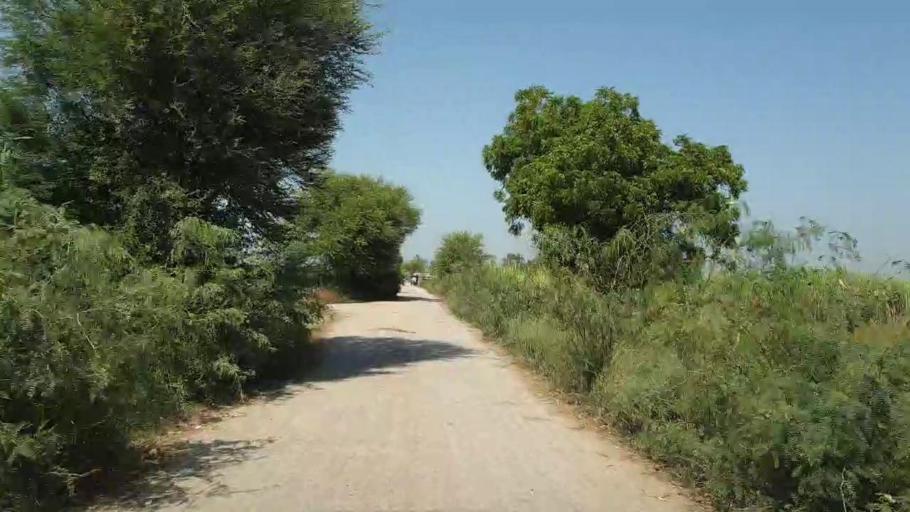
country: PK
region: Sindh
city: Tando Jam
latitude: 25.4951
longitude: 68.4637
